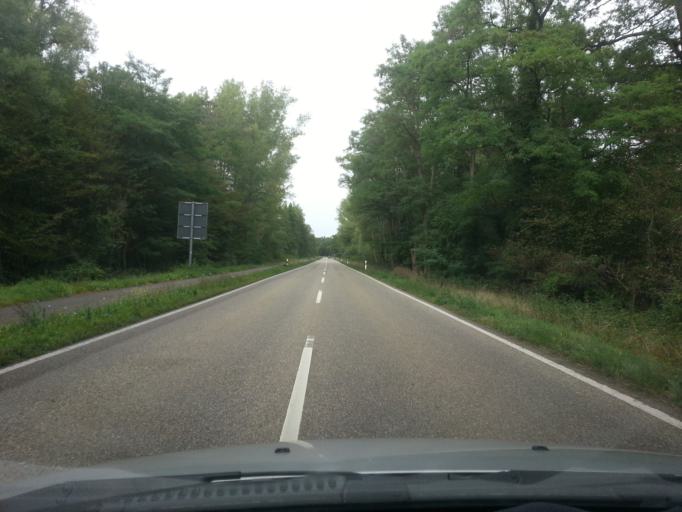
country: DE
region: Rheinland-Pfalz
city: Offenbach an der Queich
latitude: 49.2056
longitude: 8.1899
